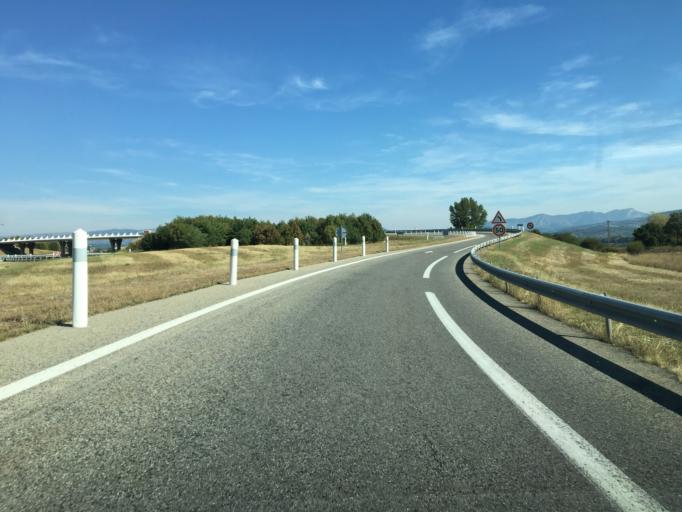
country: FR
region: Provence-Alpes-Cote d'Azur
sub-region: Departement des Alpes-de-Haute-Provence
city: Sisteron
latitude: 44.2200
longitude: 5.9197
